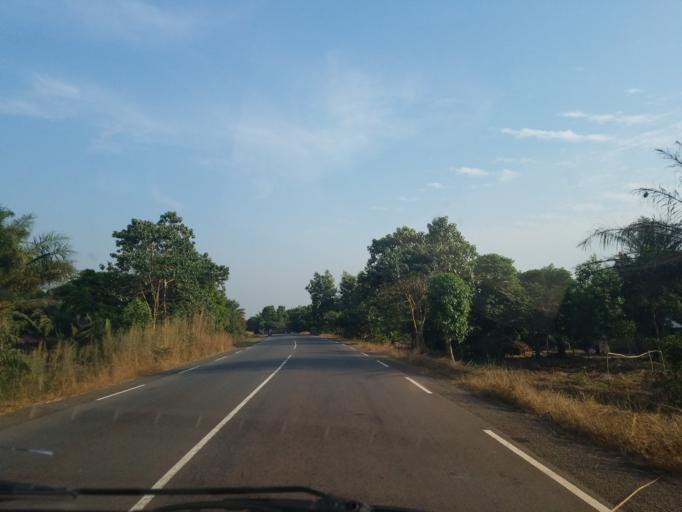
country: GN
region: Boke
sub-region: Boke Prefecture
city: Sangueya
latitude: 10.3779
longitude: -14.3126
